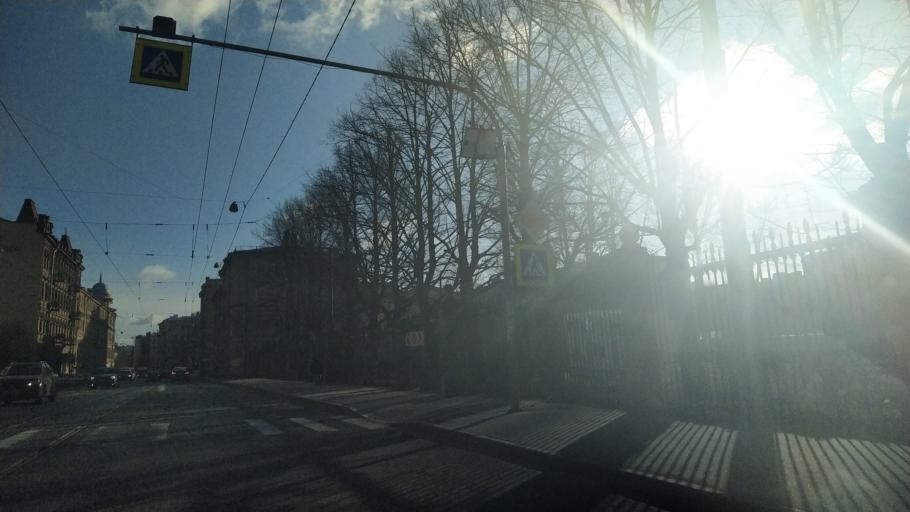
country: RU
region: Leningrad
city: Finlyandskiy
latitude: 59.9644
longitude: 30.3512
